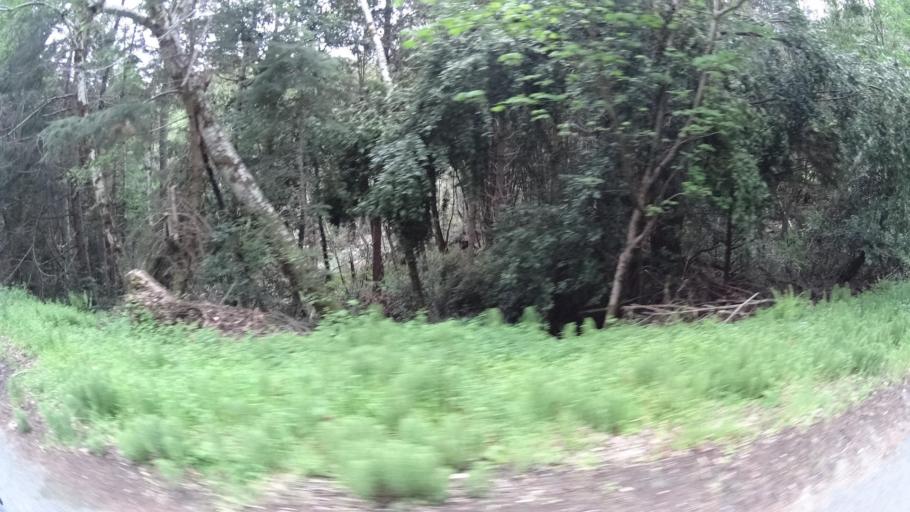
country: US
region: California
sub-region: Humboldt County
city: Blue Lake
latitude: 40.9383
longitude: -123.8453
